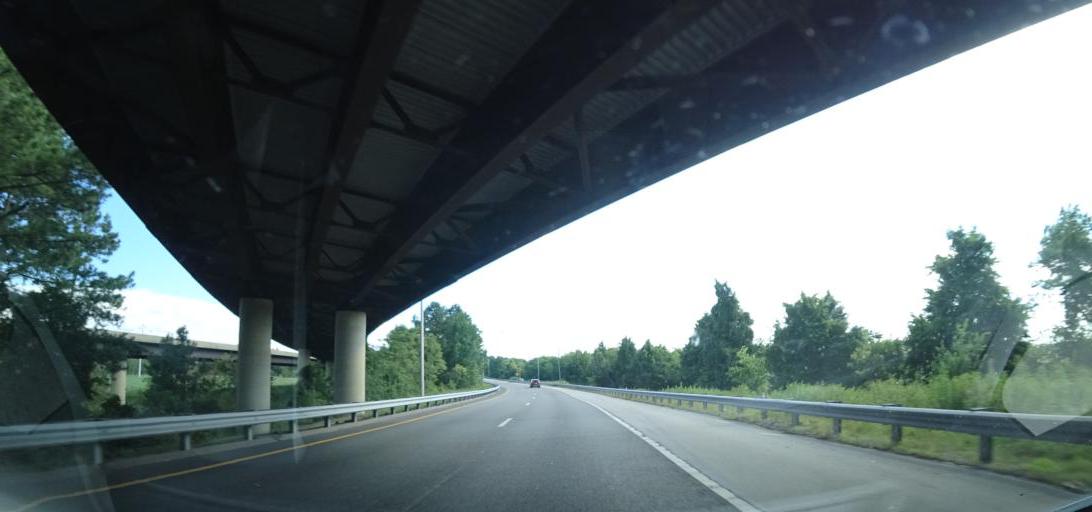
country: US
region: Virginia
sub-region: City of Hampton
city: Hampton
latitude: 37.0307
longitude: -76.3777
